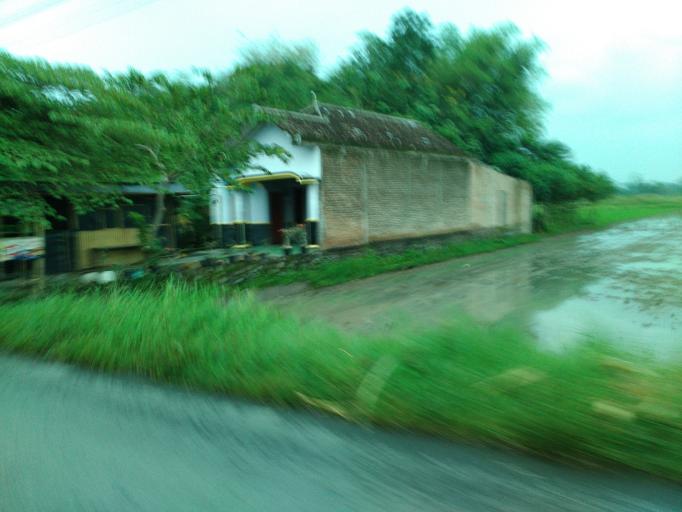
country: ID
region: Central Java
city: Ceper
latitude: -7.6518
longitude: 110.6865
